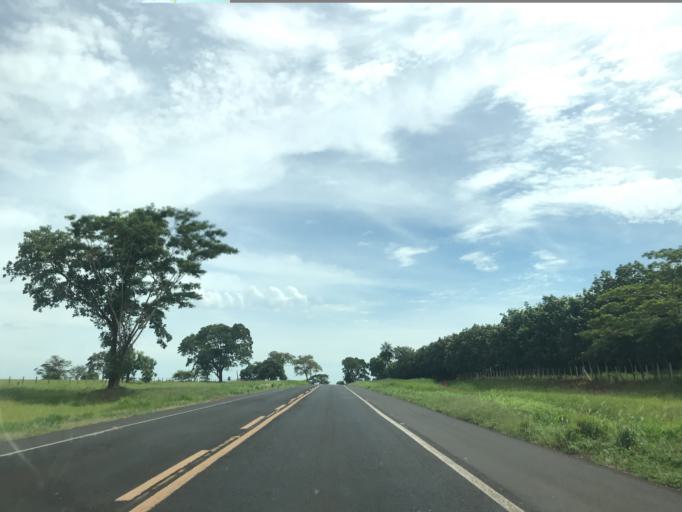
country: BR
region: Sao Paulo
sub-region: Nova Granada
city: Nova Granada
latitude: -20.3966
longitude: -49.2410
